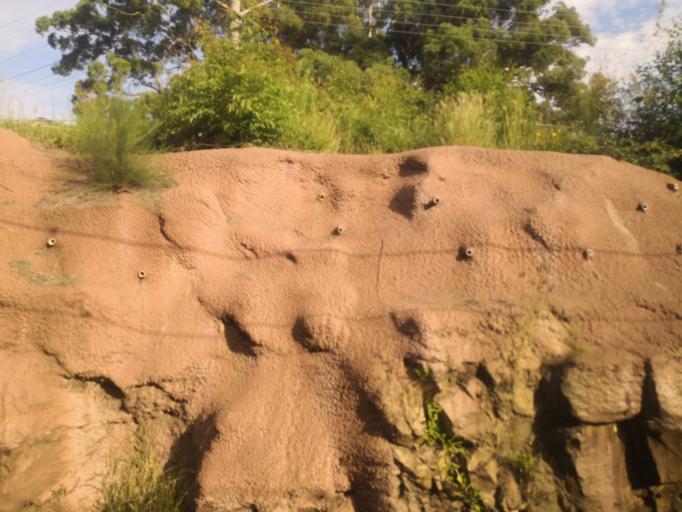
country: AU
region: New South Wales
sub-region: Gosford Shire
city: Point Clare
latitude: -33.4506
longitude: 151.3192
